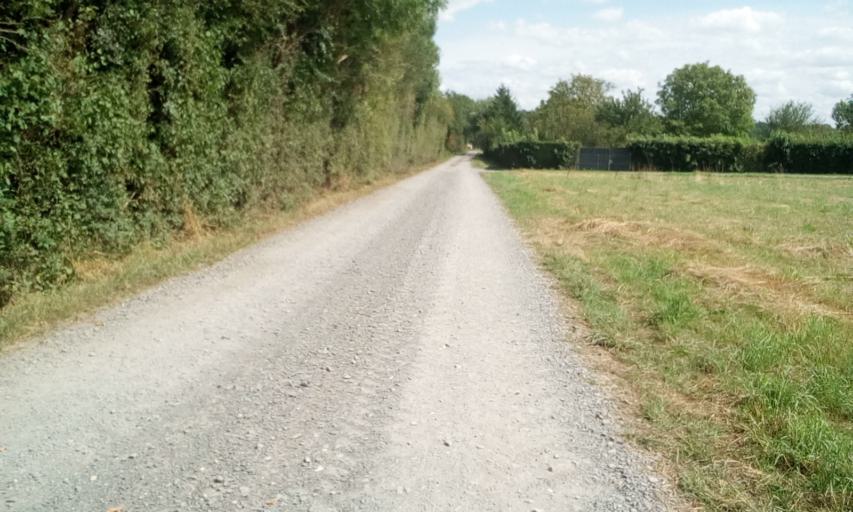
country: FR
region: Lower Normandy
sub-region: Departement du Calvados
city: Argences
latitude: 49.1344
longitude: -0.1786
